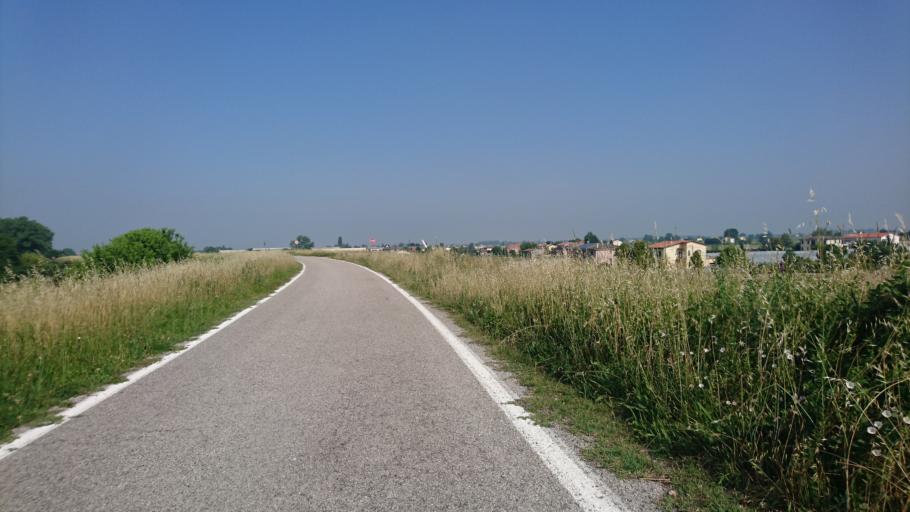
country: IT
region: Lombardy
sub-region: Provincia di Mantova
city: Borgofranco sul Po
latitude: 45.0591
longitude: 11.2172
